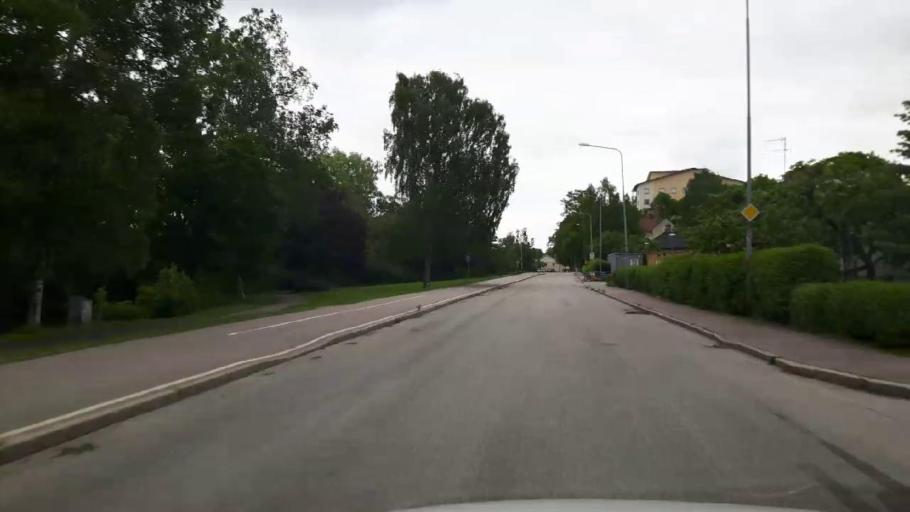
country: SE
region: Vaestmanland
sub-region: Kopings Kommun
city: Koping
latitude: 59.5177
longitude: 15.9855
